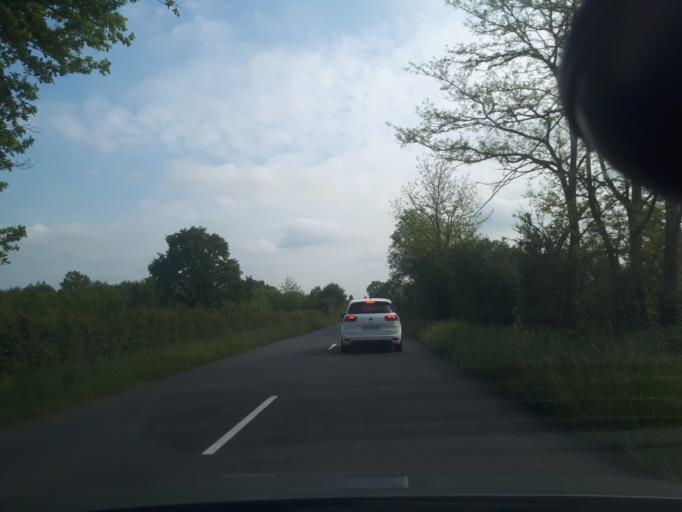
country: FR
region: Auvergne
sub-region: Departement de l'Allier
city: Dompierre-sur-Besbre
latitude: 46.4386
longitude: 3.6254
